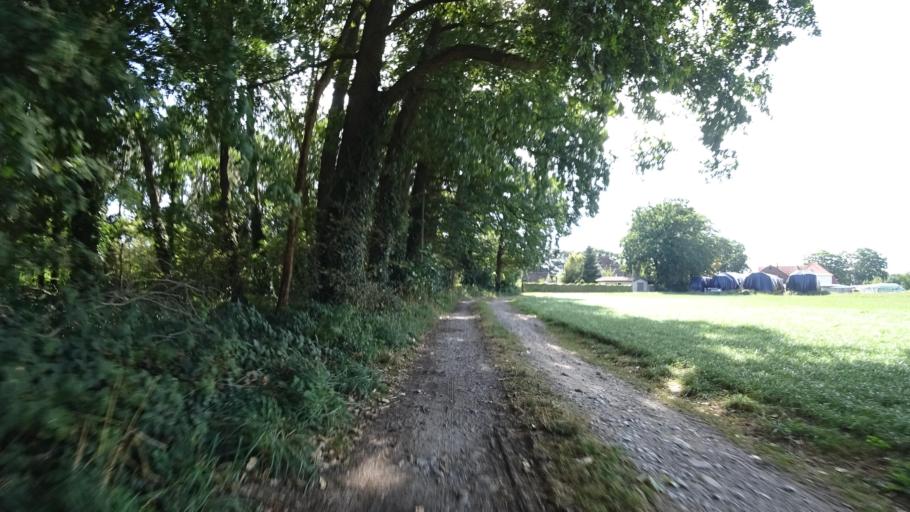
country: DE
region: North Rhine-Westphalia
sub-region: Regierungsbezirk Detmold
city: Guetersloh
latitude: 51.8874
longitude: 8.4099
